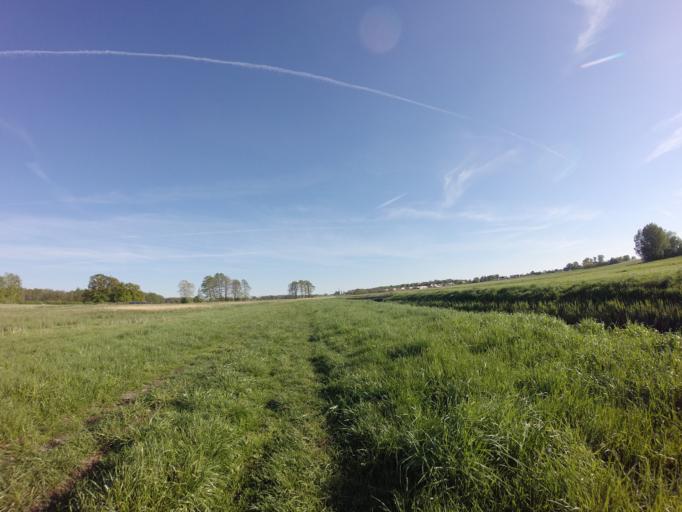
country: PL
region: West Pomeranian Voivodeship
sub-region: Powiat choszczenski
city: Pelczyce
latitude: 53.1276
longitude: 15.3290
